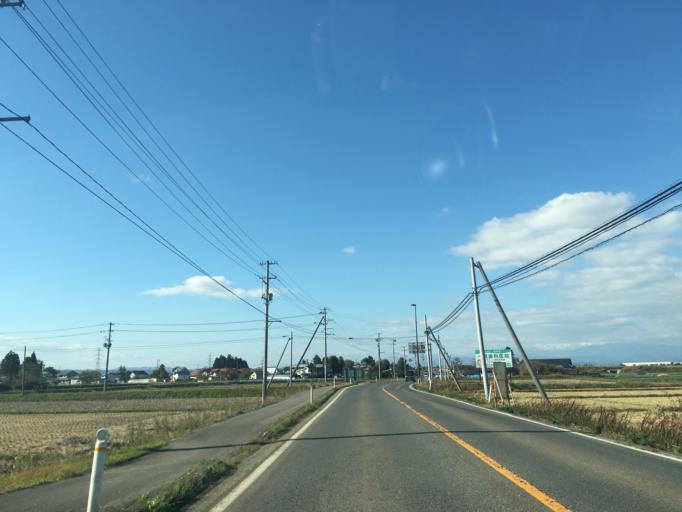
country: JP
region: Fukushima
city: Kitakata
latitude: 37.5272
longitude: 139.8882
